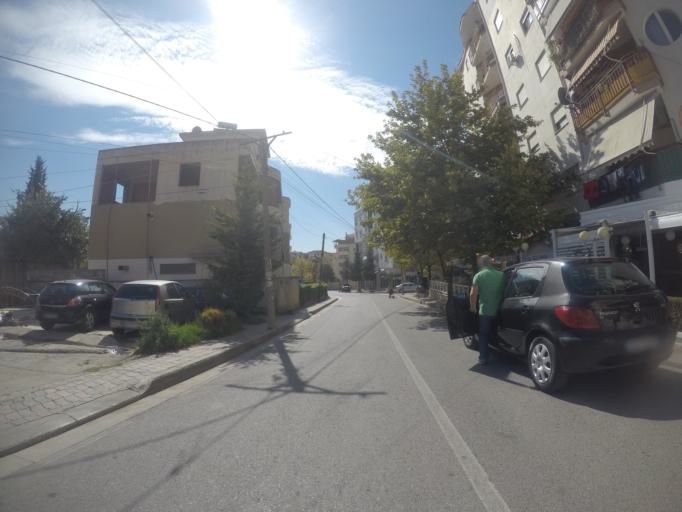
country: AL
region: Tirane
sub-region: Rrethi i Tiranes
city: Farka e Madhe
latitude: 41.3488
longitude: 19.8580
